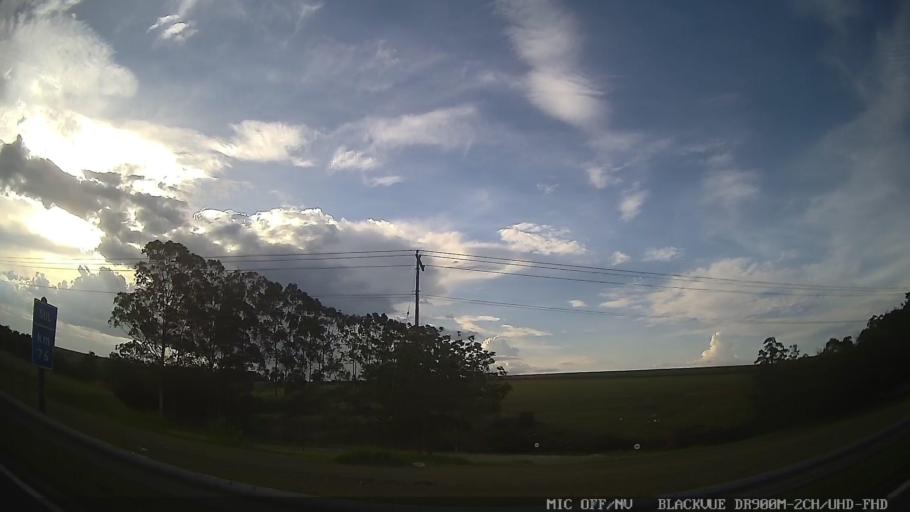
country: BR
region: Sao Paulo
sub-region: Tiete
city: Tiete
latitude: -23.0606
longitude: -47.7239
